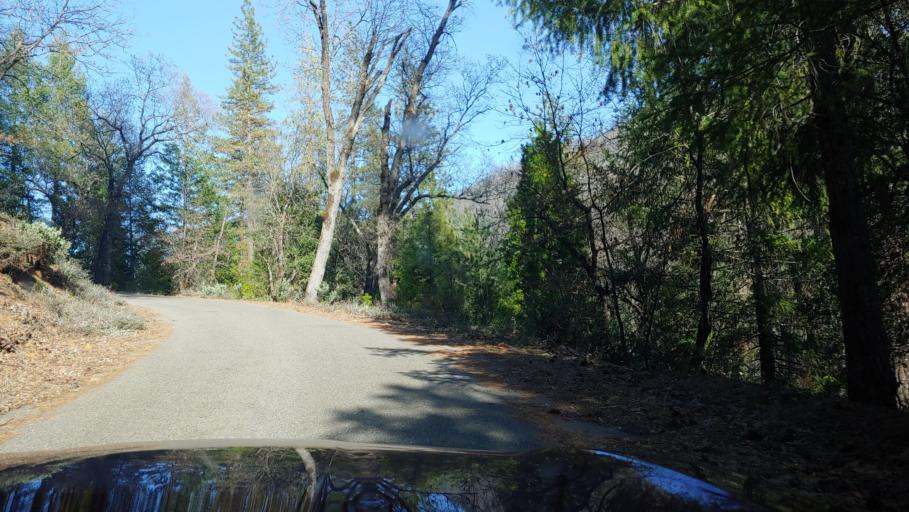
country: US
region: California
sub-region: Siskiyou County
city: Dunsmuir
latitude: 40.9972
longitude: -122.4113
